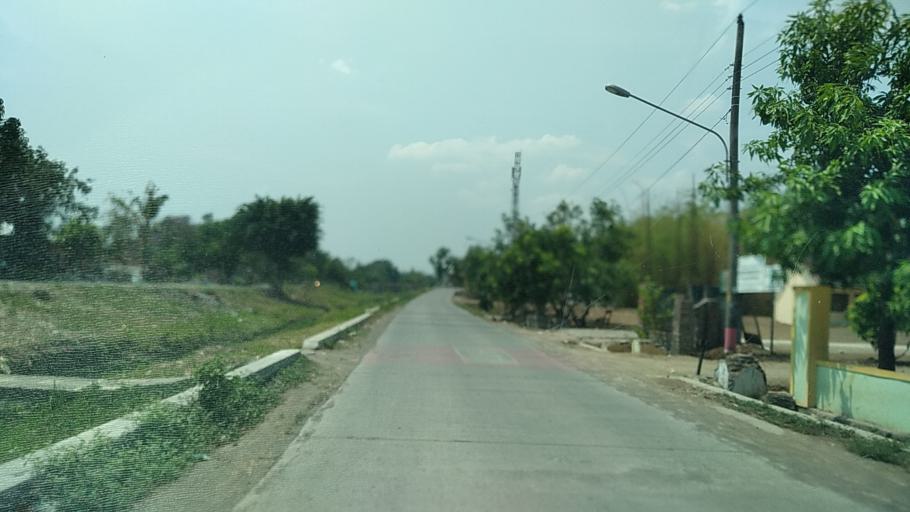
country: ID
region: Central Java
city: Mranggen
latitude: -7.0350
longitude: 110.4823
